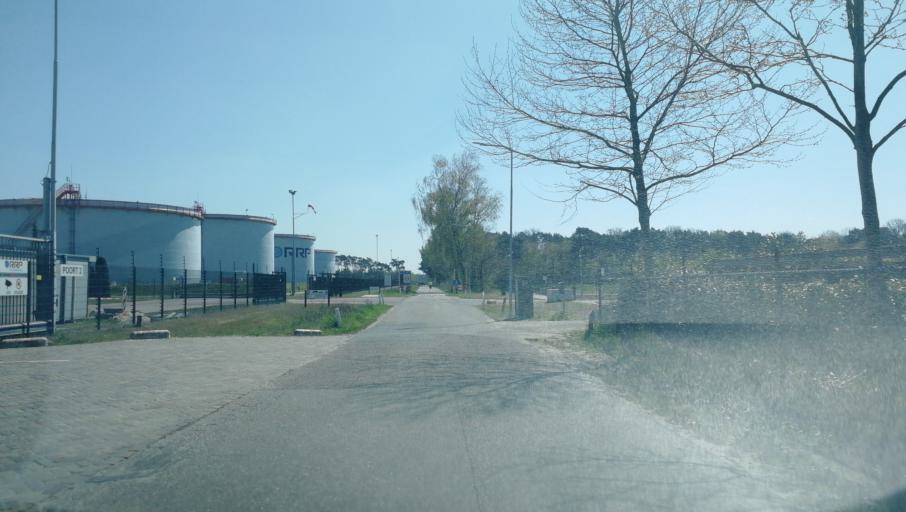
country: NL
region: Limburg
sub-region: Gemeente Venlo
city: Venlo
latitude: 51.3793
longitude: 6.2147
